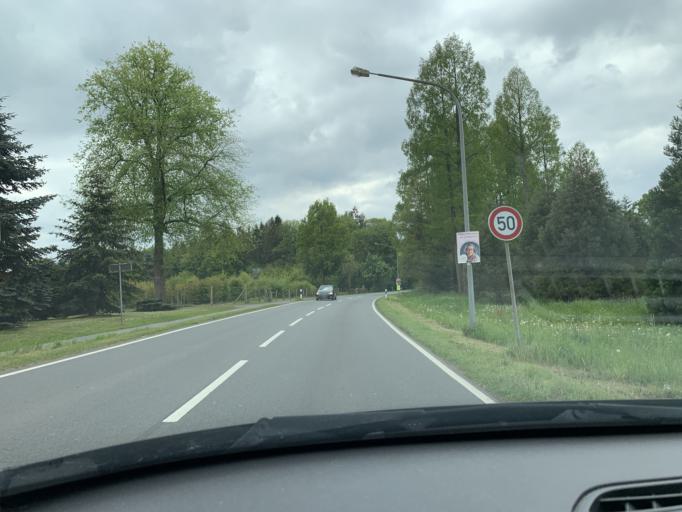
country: DE
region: Lower Saxony
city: Westerstede
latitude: 53.2495
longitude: 7.9267
